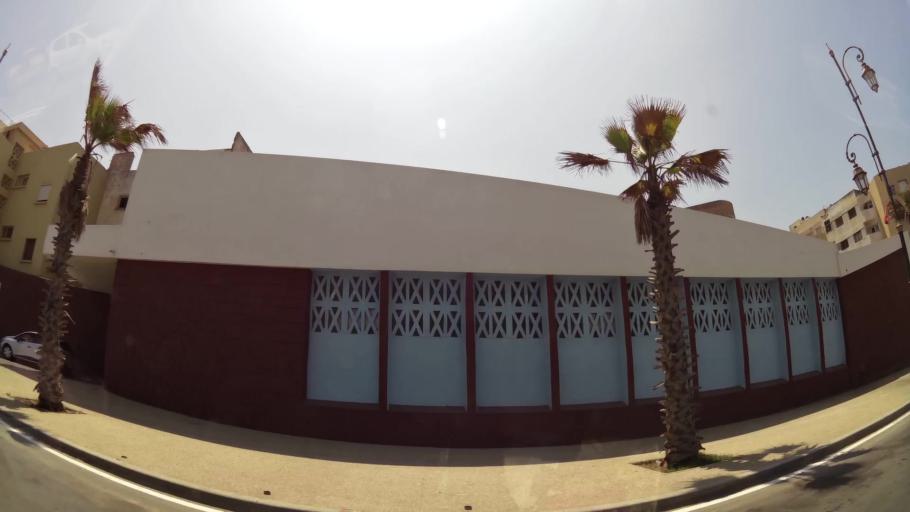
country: MA
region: Rabat-Sale-Zemmour-Zaer
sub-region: Rabat
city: Rabat
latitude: 34.0264
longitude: -6.8490
